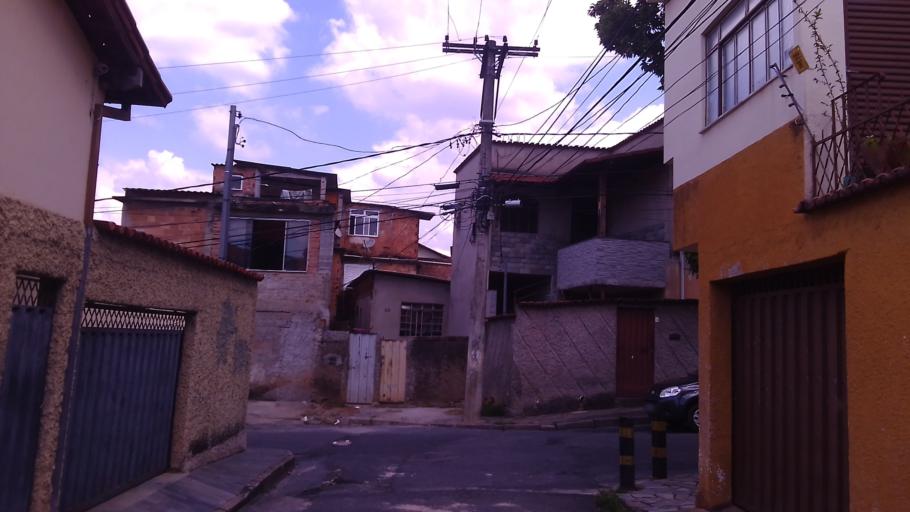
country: BR
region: Minas Gerais
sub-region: Belo Horizonte
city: Belo Horizonte
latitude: -19.8995
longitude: -43.9145
